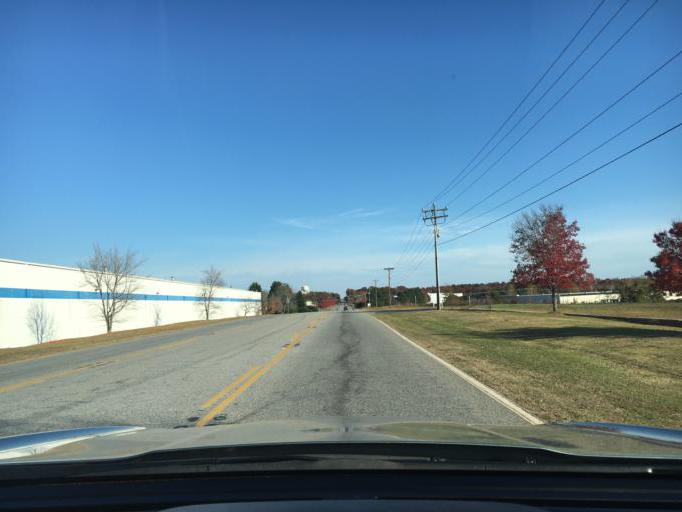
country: US
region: South Carolina
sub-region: Spartanburg County
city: Southern Shops
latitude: 34.9938
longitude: -82.0404
